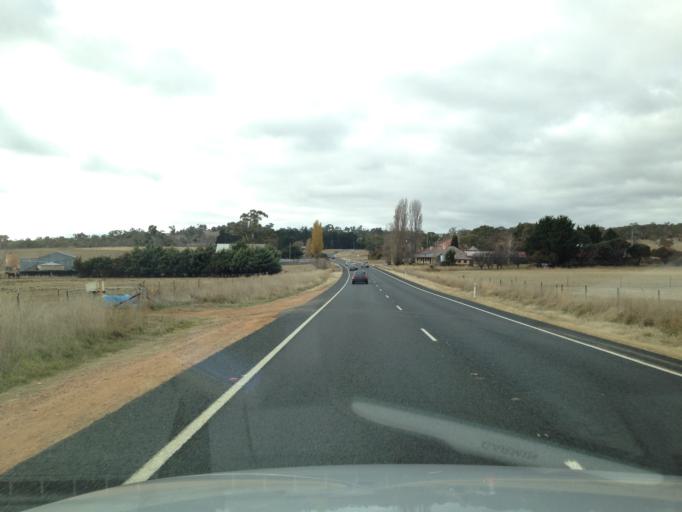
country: AU
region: New South Wales
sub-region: Cooma-Monaro
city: Cooma
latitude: -36.2436
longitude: 149.0602
